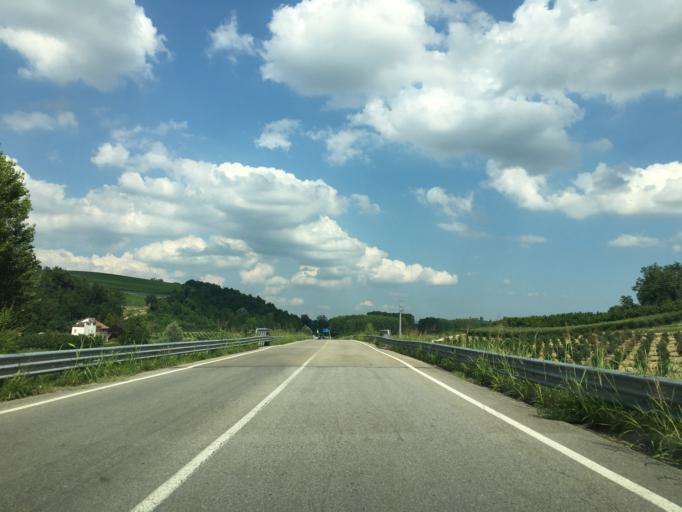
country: IT
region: Piedmont
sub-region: Provincia di Cuneo
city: Piobesi d'Alba
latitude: 44.7299
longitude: 7.9834
